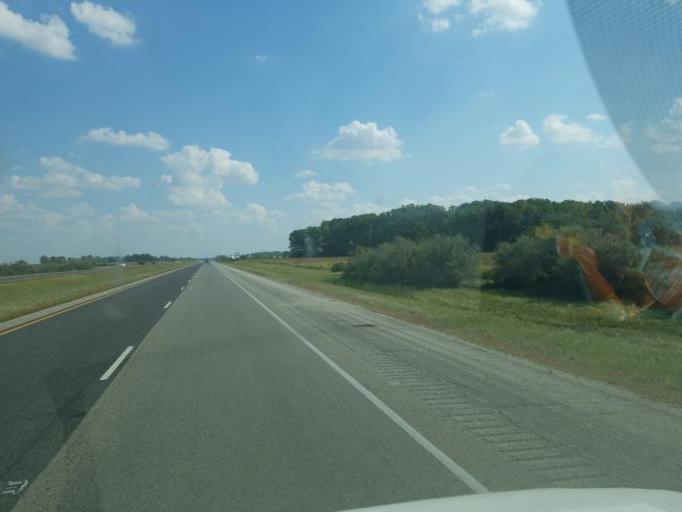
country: US
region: Indiana
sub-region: Allen County
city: Monroeville
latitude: 41.0118
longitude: -84.8574
